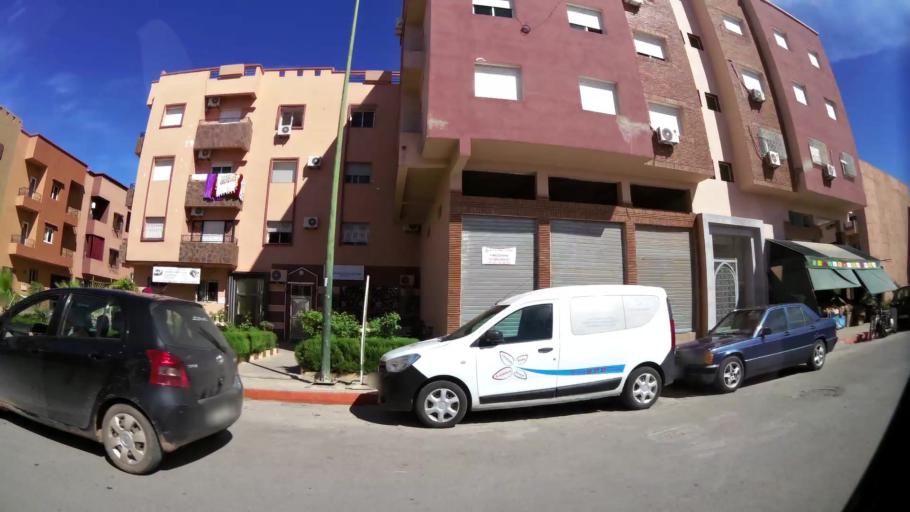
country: MA
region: Marrakech-Tensift-Al Haouz
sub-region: Marrakech
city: Marrakesh
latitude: 31.6711
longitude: -8.0219
